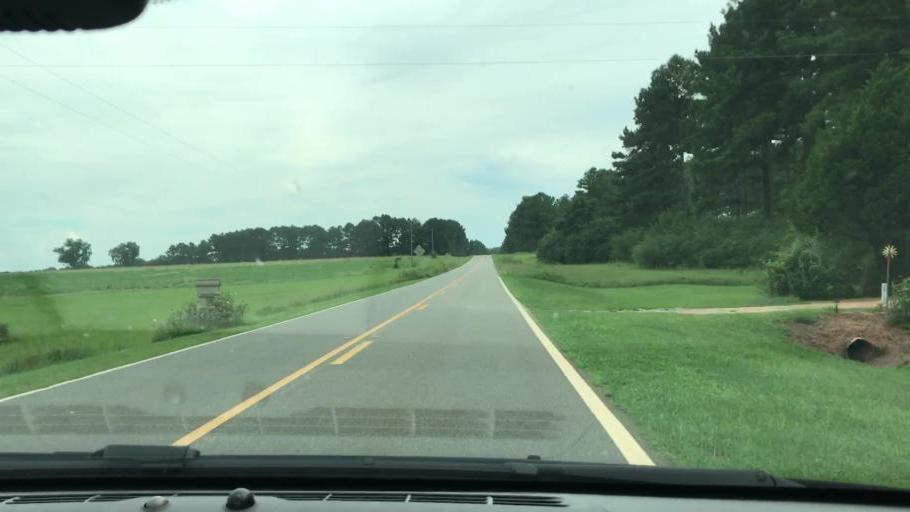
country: US
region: Georgia
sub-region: Early County
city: Blakely
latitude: 31.4507
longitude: -84.9132
